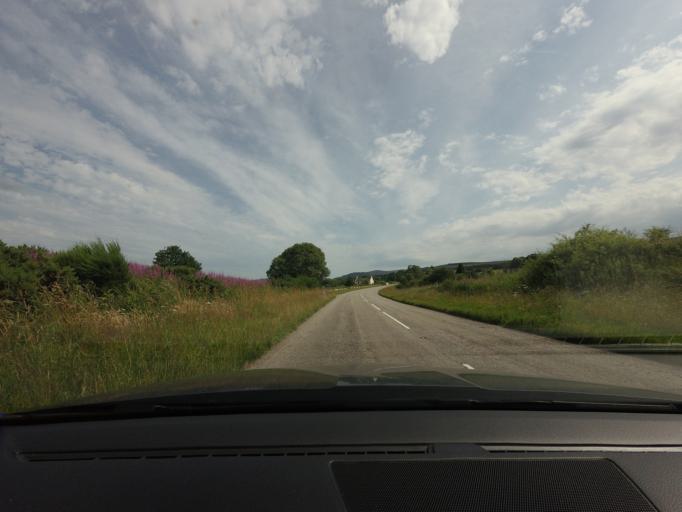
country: GB
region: Scotland
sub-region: Highland
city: Alness
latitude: 57.8748
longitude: -4.3554
